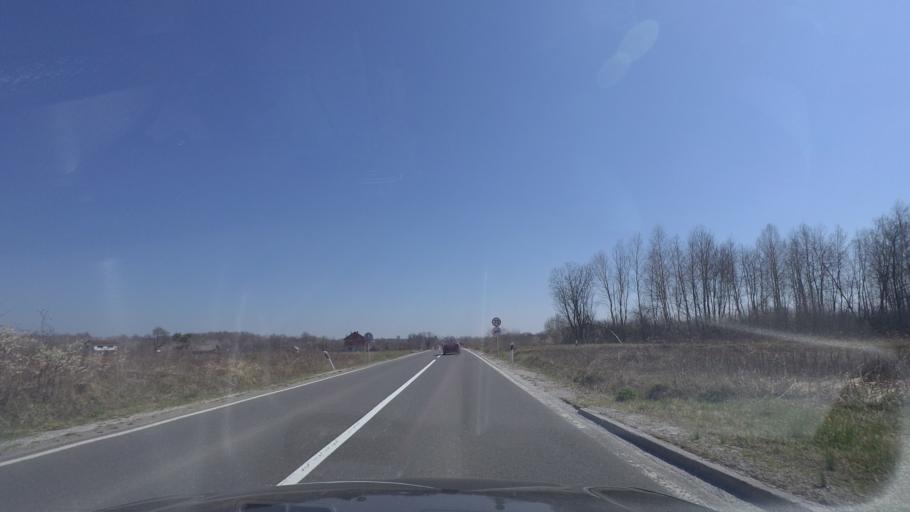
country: HR
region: Sisacko-Moslavacka
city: Gvozd
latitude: 45.3355
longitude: 15.9099
